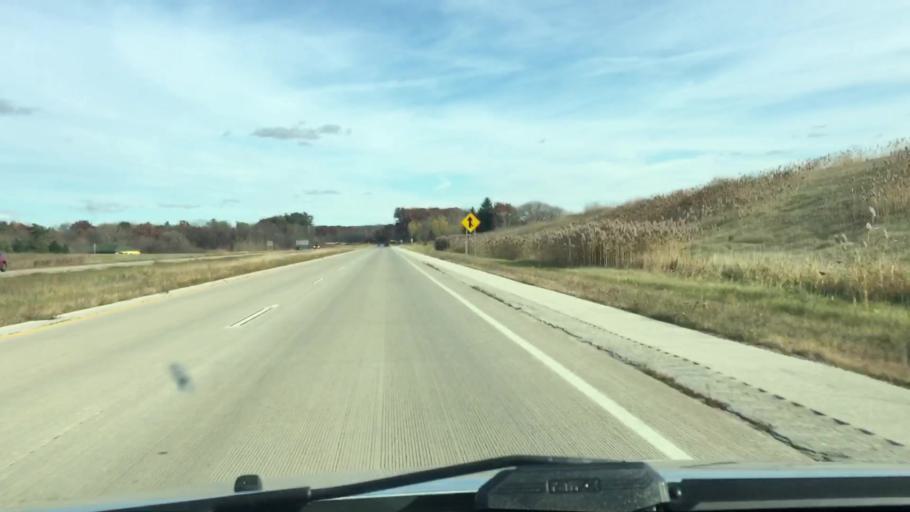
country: US
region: Wisconsin
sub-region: Kewaunee County
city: Luxemburg
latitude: 44.6338
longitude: -87.7751
